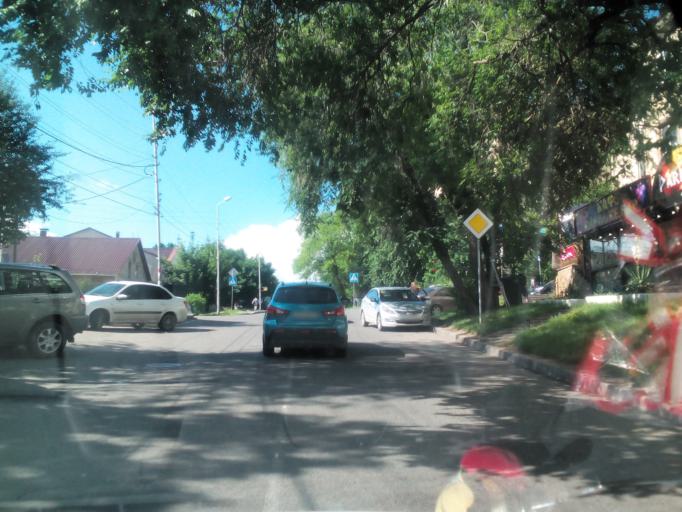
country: RU
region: Stavropol'skiy
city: Pyatigorsk
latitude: 44.0447
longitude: 43.0688
